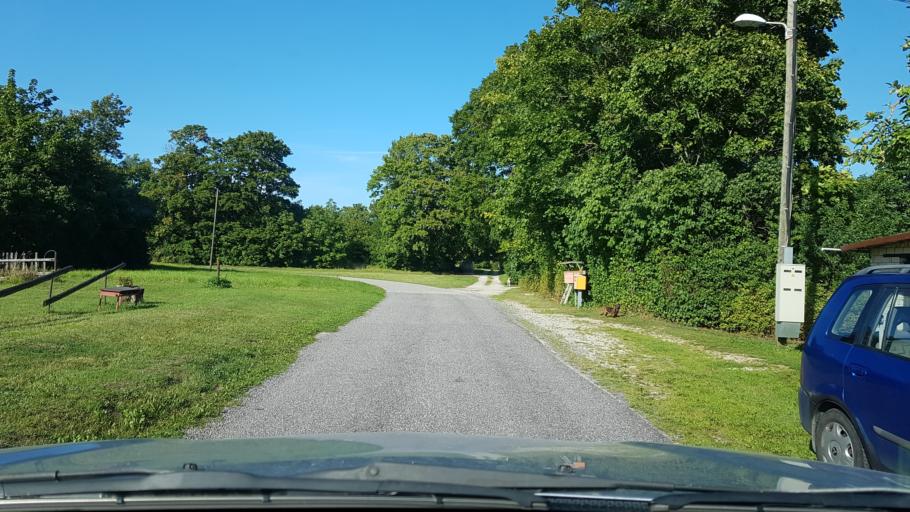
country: EE
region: Ida-Virumaa
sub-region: Narva-Joesuu linn
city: Narva-Joesuu
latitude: 59.4032
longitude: 28.0022
